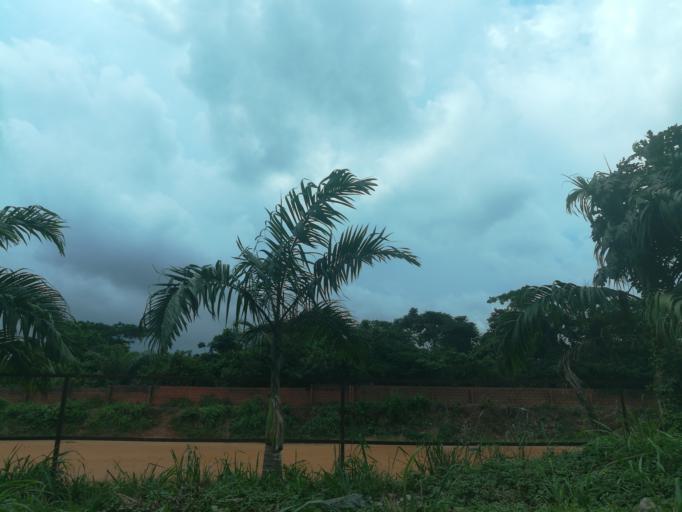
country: NG
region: Lagos
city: Ikorodu
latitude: 6.6416
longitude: 3.5509
